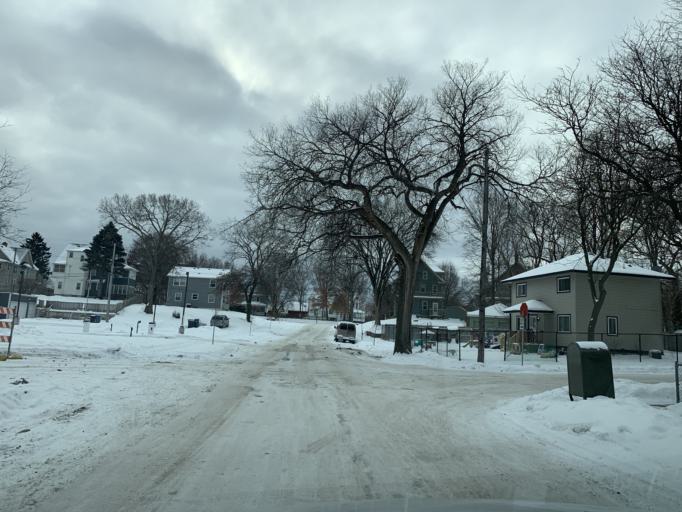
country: US
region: Minnesota
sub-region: Hennepin County
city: Minneapolis
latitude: 44.9866
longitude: -93.2997
